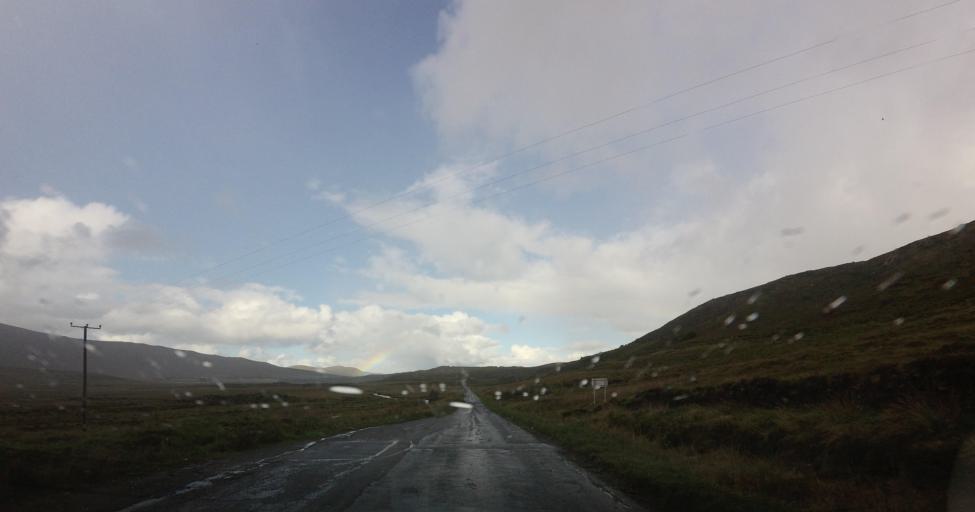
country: GB
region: Scotland
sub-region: Highland
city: Portree
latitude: 57.2204
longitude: -5.9371
